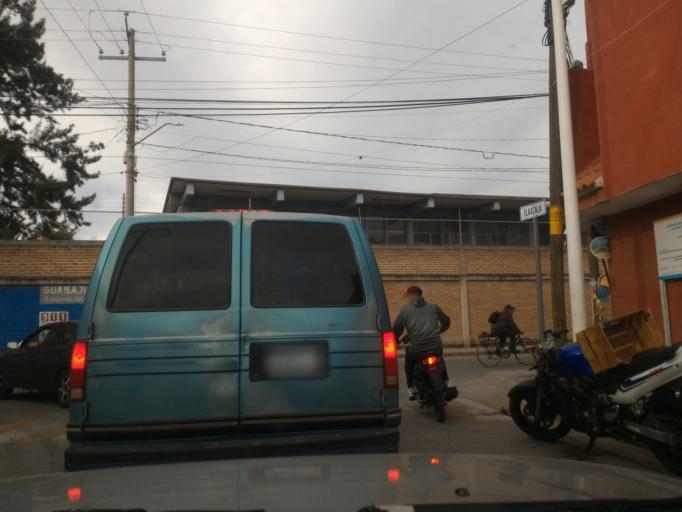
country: MX
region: Guanajuato
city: San Francisco del Rincon
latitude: 21.0088
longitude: -101.8507
